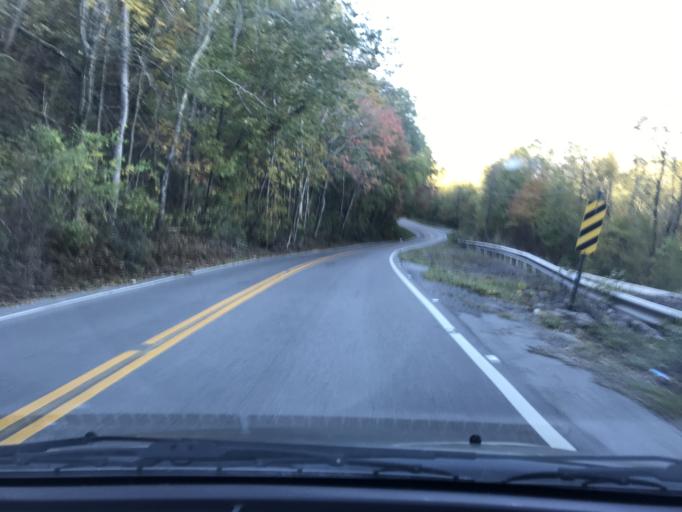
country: US
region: Georgia
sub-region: Dade County
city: Trenton
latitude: 34.9019
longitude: -85.4431
